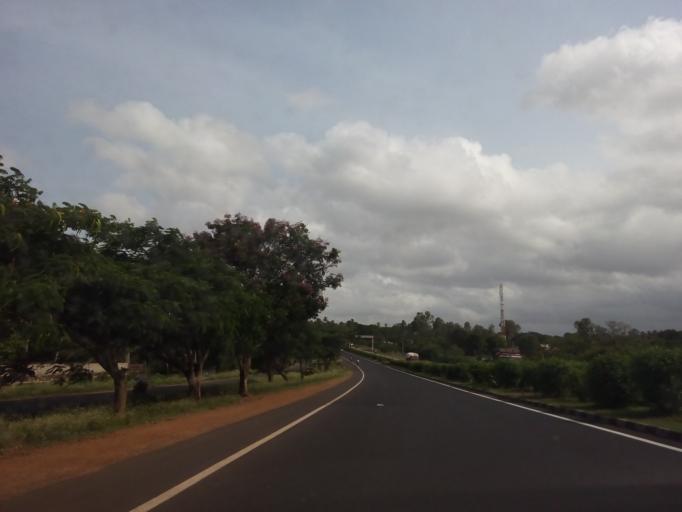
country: IN
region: Karnataka
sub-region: Belgaum
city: Sankeshwar
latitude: 16.1326
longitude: 74.5163
